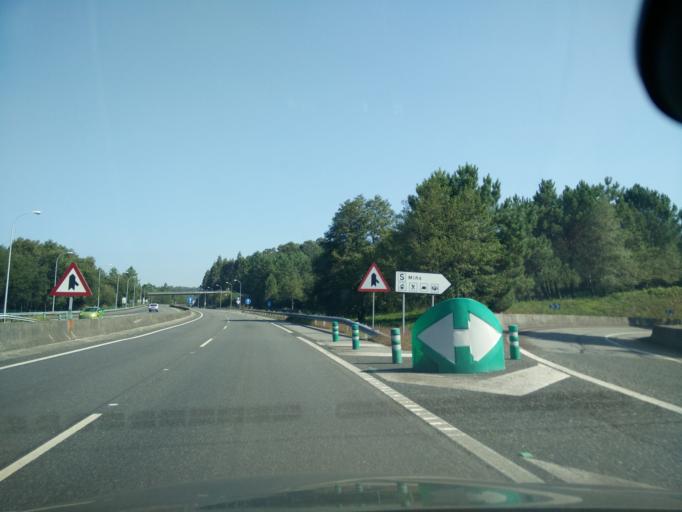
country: ES
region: Galicia
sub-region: Provincia da Coruna
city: Mino
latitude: 43.3748
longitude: -8.1849
